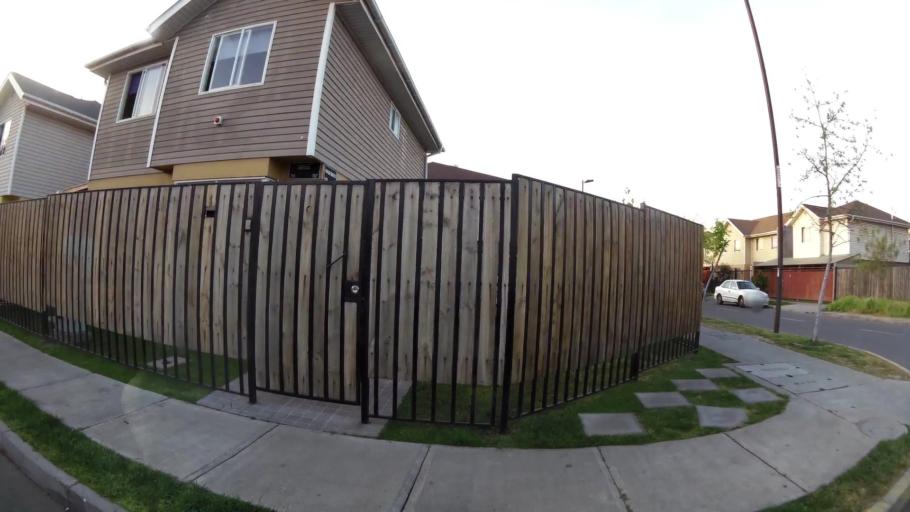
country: CL
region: Santiago Metropolitan
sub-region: Provincia de Cordillera
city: Puente Alto
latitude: -33.5970
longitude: -70.5870
